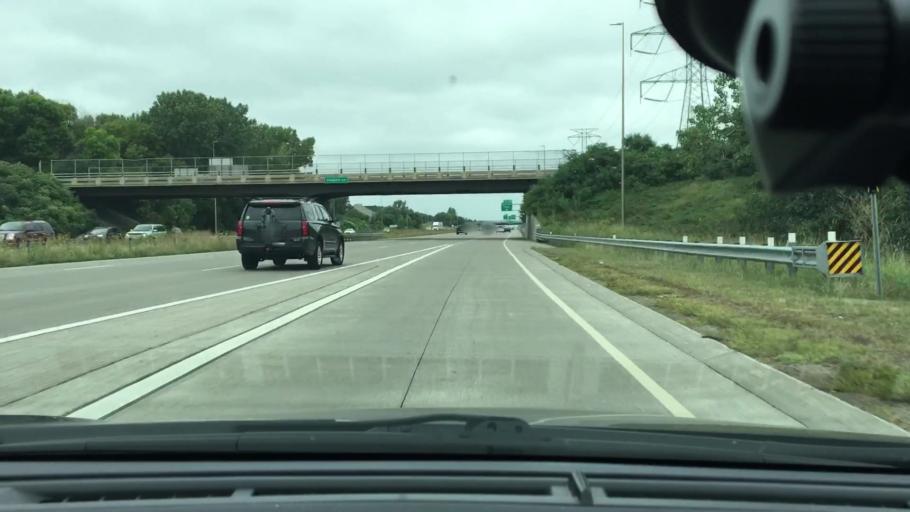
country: US
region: Minnesota
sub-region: Hennepin County
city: Plymouth
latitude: 44.9748
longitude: -93.4601
